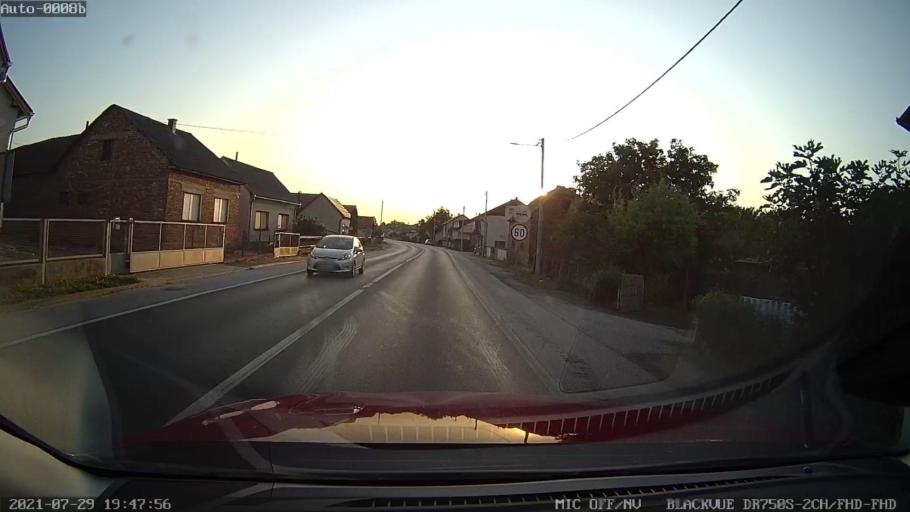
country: HR
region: Varazdinska
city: Ludbreg
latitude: 46.2645
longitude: 16.5546
